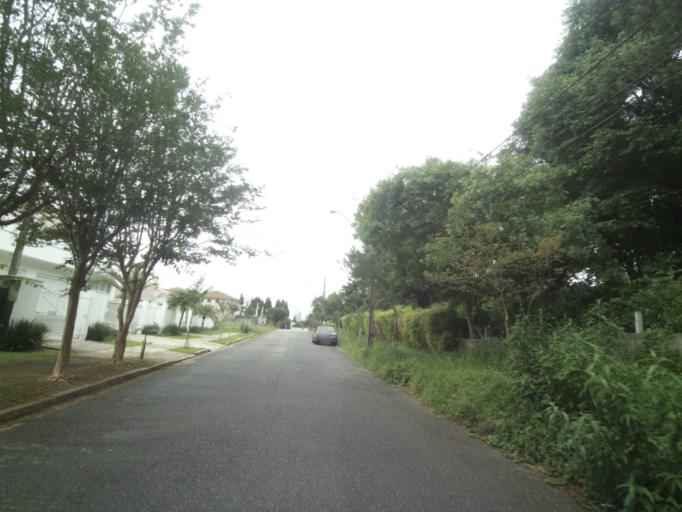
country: BR
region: Parana
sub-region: Curitiba
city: Curitiba
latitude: -25.4039
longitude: -49.2854
